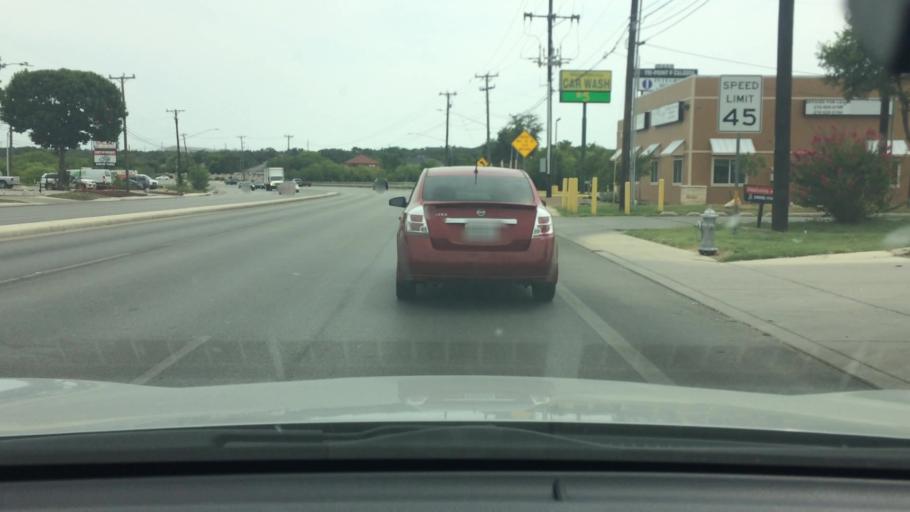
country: US
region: Texas
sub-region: Bexar County
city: Leon Valley
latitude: 29.4841
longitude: -98.6668
